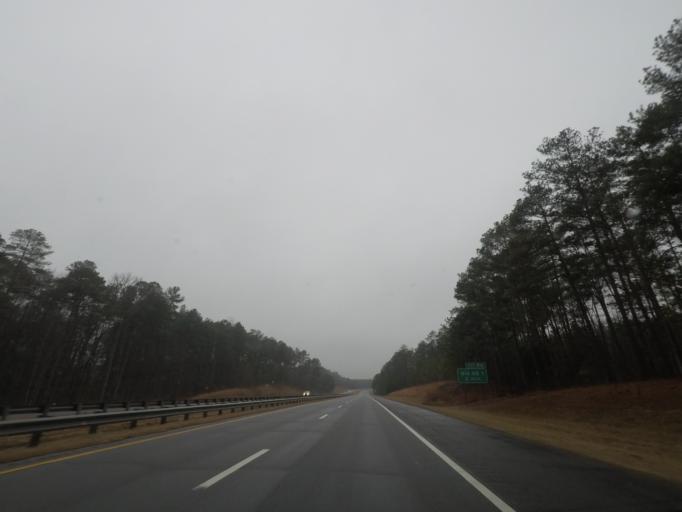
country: US
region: North Carolina
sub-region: Wake County
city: Holly Springs
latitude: 35.6491
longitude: -78.9701
